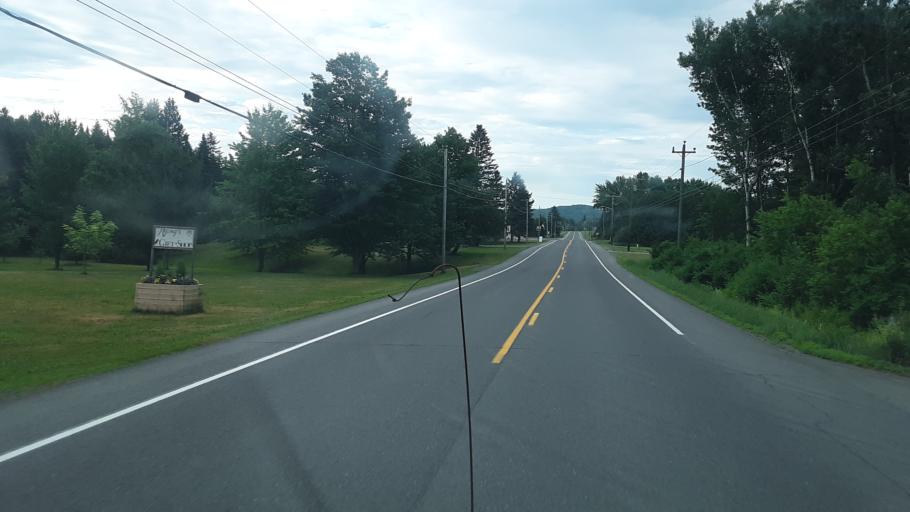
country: US
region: Maine
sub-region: Penobscot County
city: Patten
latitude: 45.9125
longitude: -68.4377
